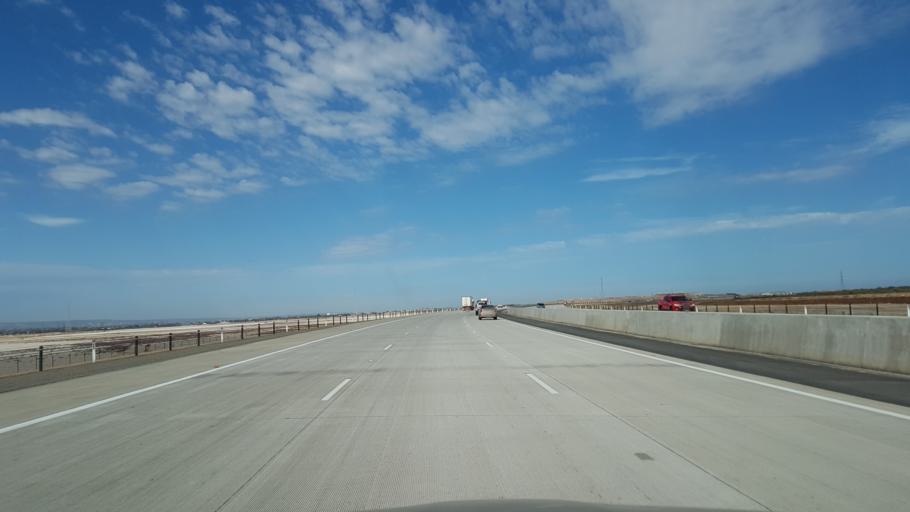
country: AU
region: South Australia
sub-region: Port Adelaide Enfield
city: Enfield
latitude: -34.8002
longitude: 138.5767
